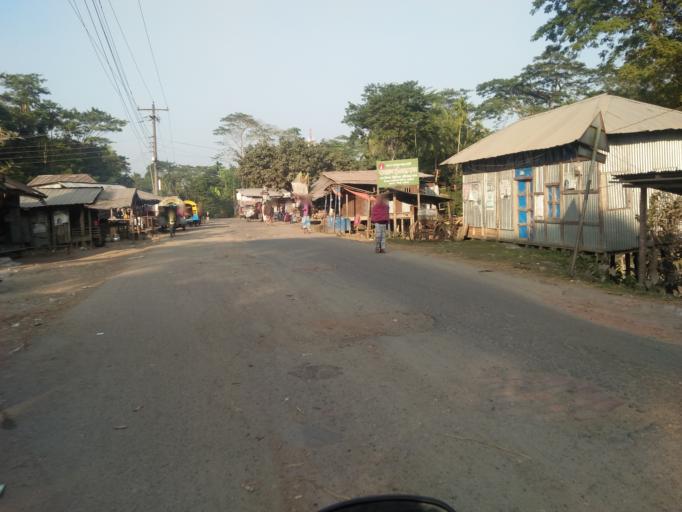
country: BD
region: Barisal
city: Bhola
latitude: 22.7504
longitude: 90.6350
